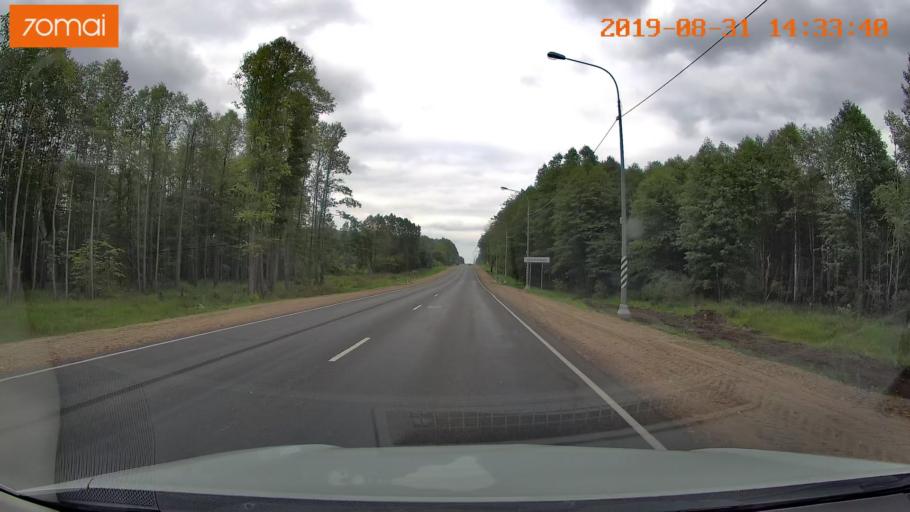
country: RU
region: Smolensk
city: Yekimovichi
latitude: 54.1534
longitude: 33.4240
